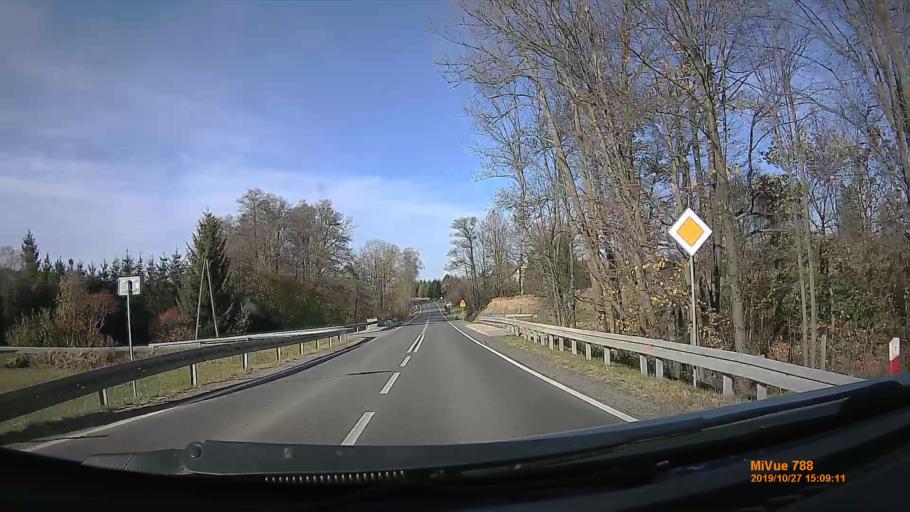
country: PL
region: Lower Silesian Voivodeship
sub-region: Powiat klodzki
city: Miedzylesie
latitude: 50.1774
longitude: 16.6696
